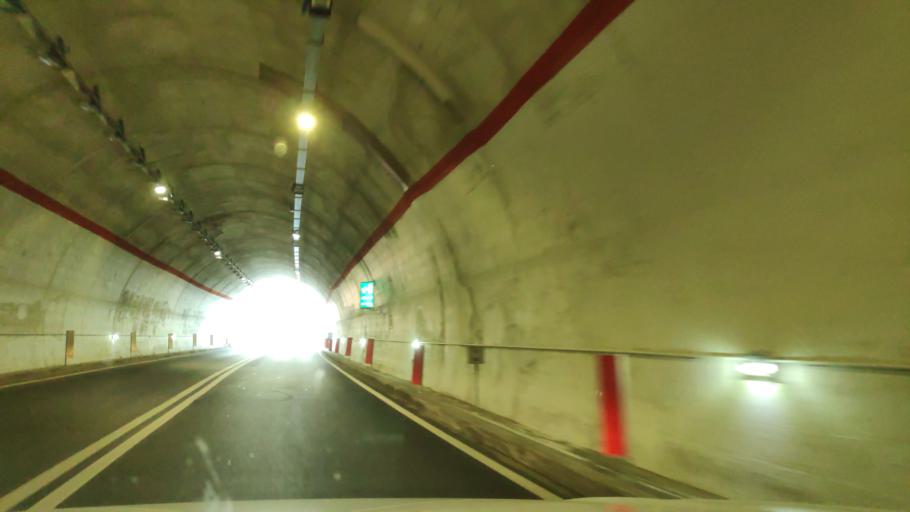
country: IT
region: Calabria
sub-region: Provincia di Reggio Calabria
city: Bova Marina
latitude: 37.9259
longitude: 15.9455
